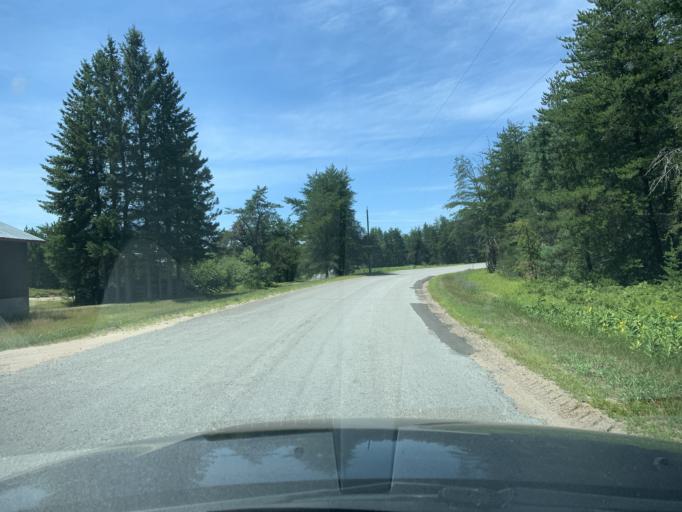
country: CA
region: Ontario
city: Petawawa
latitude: 45.6582
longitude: -77.6020
